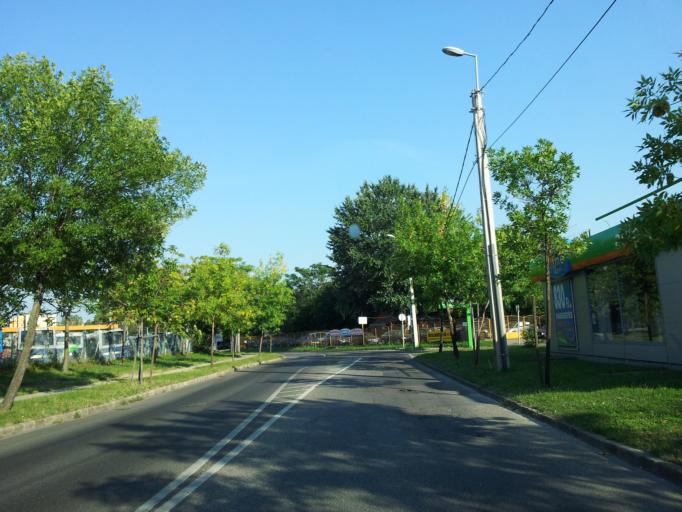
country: HU
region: Budapest
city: Budapest XI. keruelet
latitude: 47.4732
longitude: 19.0271
